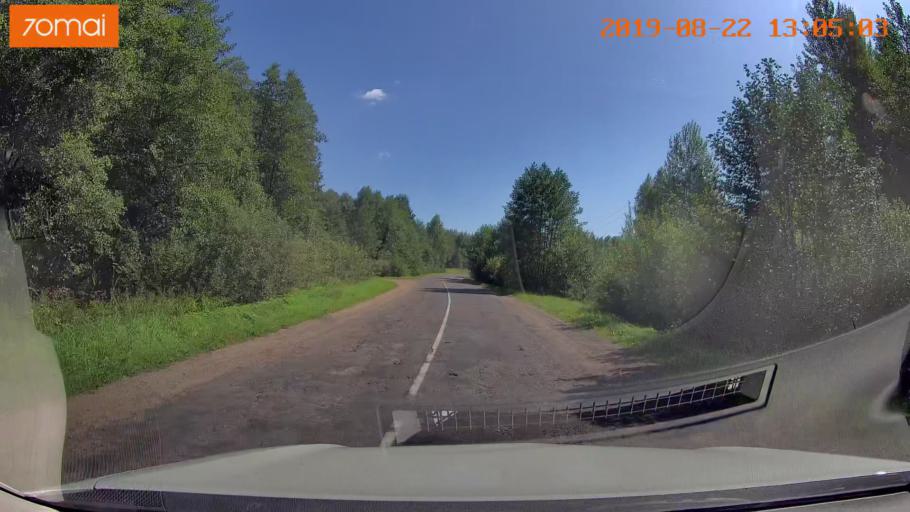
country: BY
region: Minsk
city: Prawdzinski
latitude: 53.3630
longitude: 27.8304
